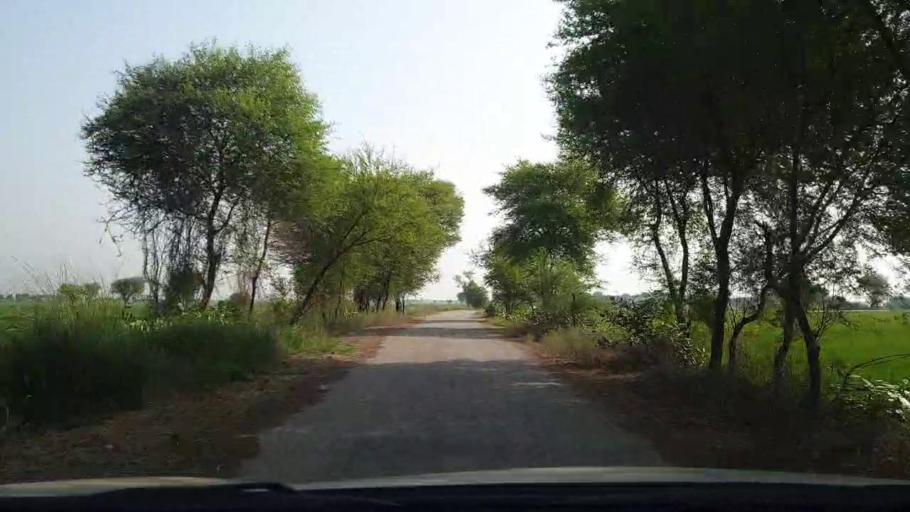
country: PK
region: Sindh
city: Goth Garelo
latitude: 27.4749
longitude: 68.1191
